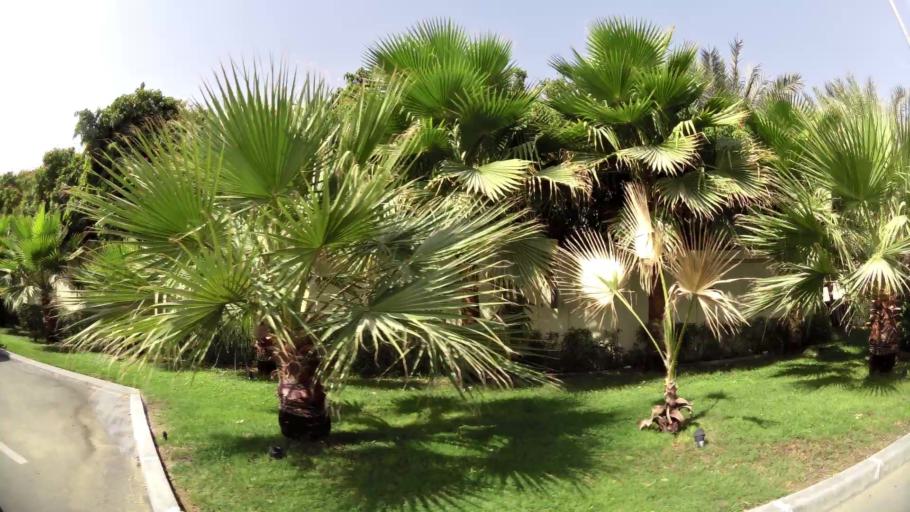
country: AE
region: Ash Shariqah
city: Sharjah
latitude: 25.2036
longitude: 55.4045
